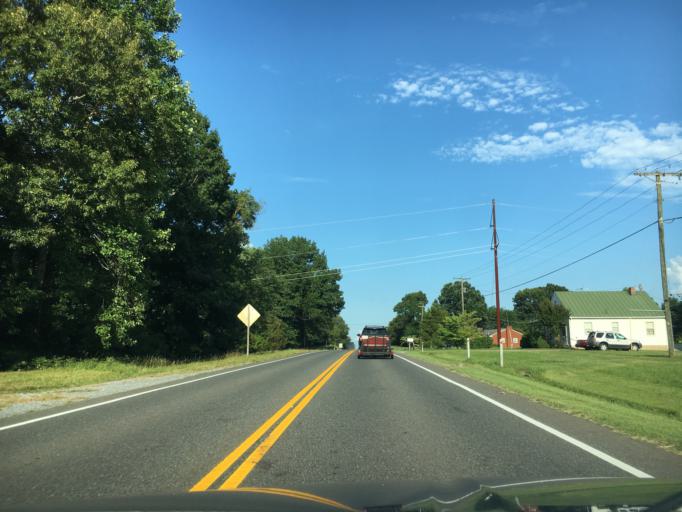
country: US
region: Virginia
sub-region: Bedford County
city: Forest
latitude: 37.3751
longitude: -79.3307
